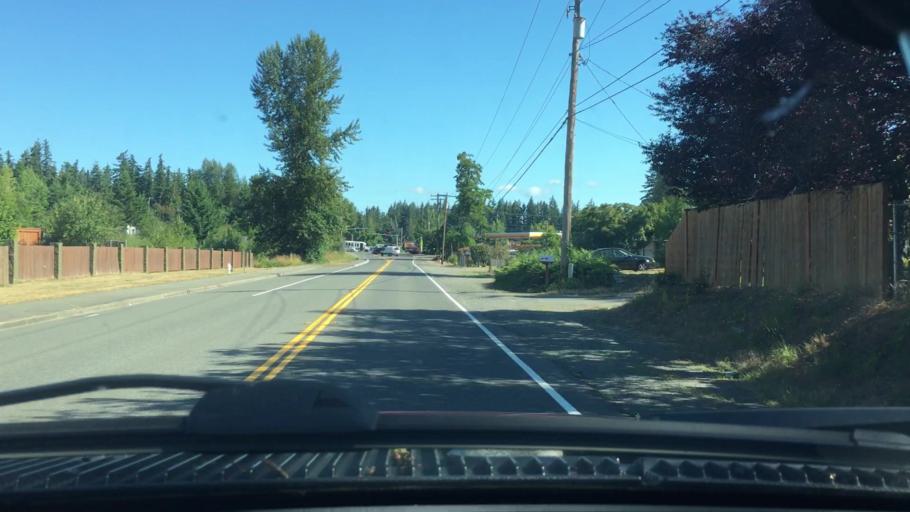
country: US
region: Washington
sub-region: King County
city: Covington
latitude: 47.3558
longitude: -122.1389
